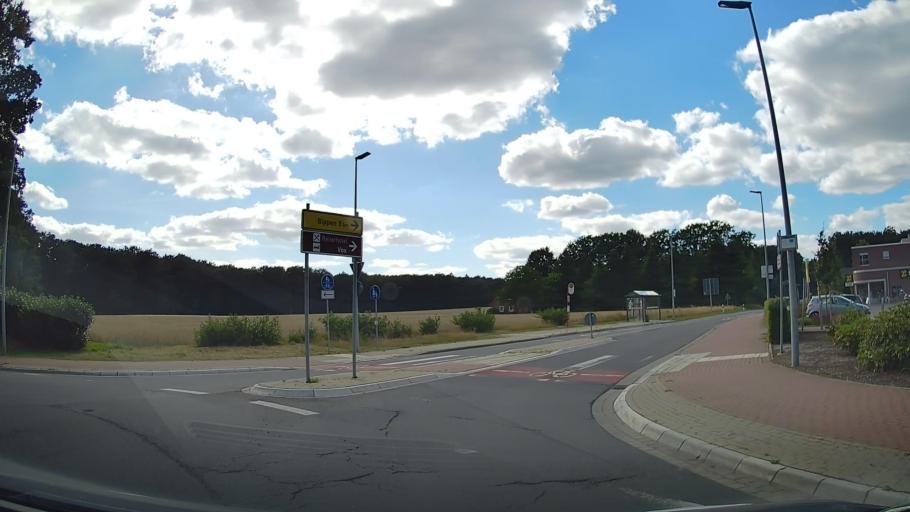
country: DE
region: Lower Saxony
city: Eggermuhlen
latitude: 52.5664
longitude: 7.8157
